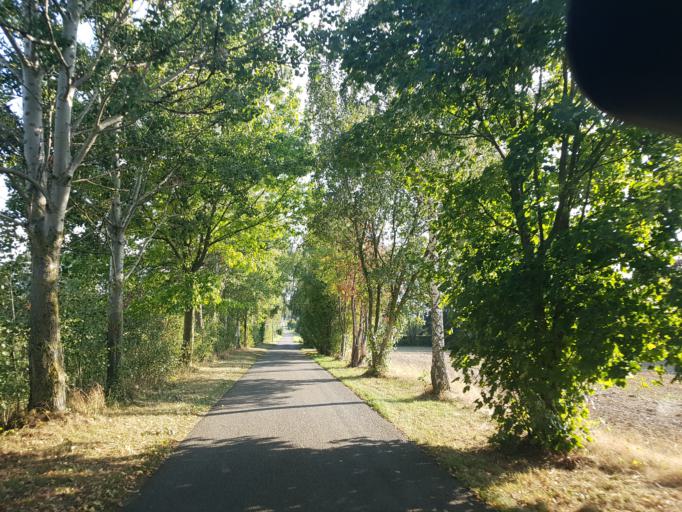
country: DE
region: Saxony
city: Dobeln
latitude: 51.1086
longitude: 13.0906
